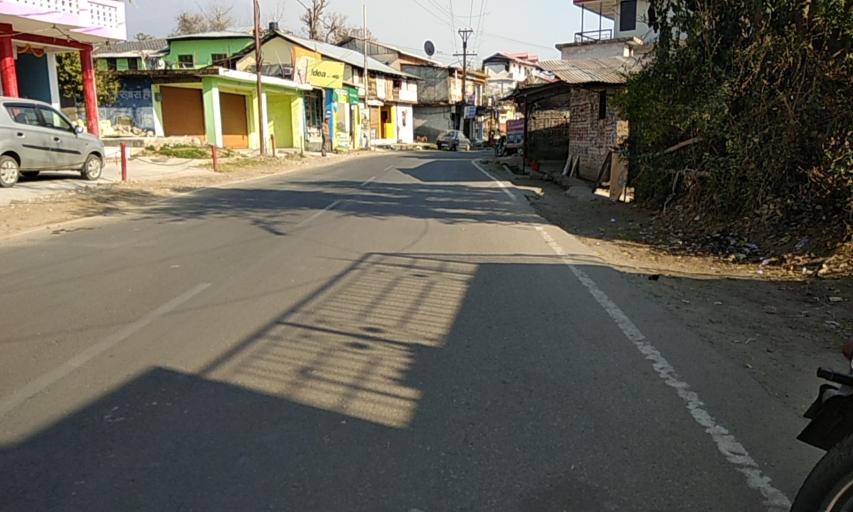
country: IN
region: Himachal Pradesh
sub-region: Kangra
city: Palampur
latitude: 32.1134
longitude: 76.5286
